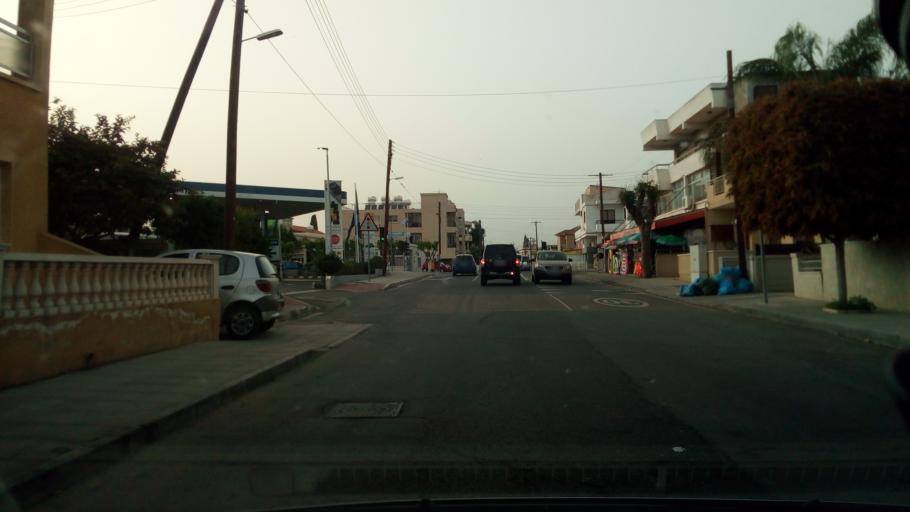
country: CY
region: Limassol
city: Limassol
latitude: 34.6582
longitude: 33.0034
